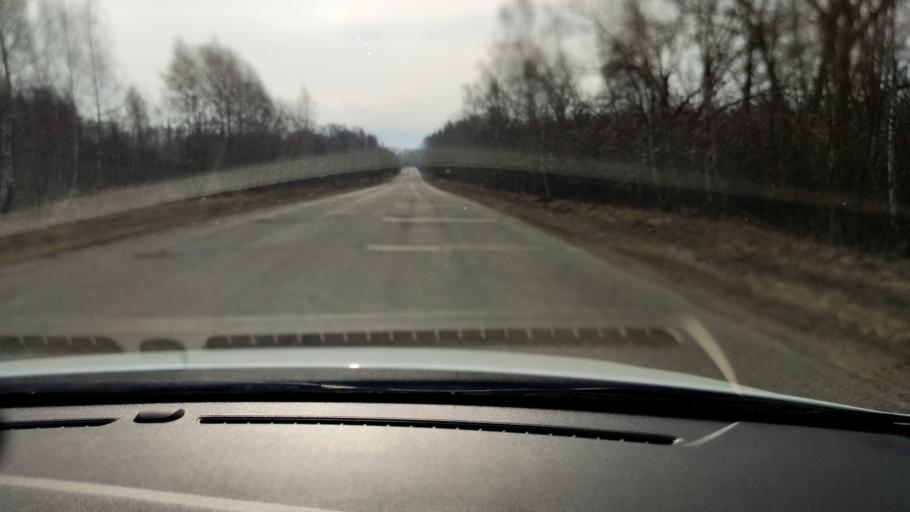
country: RU
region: Tatarstan
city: Stolbishchi
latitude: 55.7189
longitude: 49.2150
